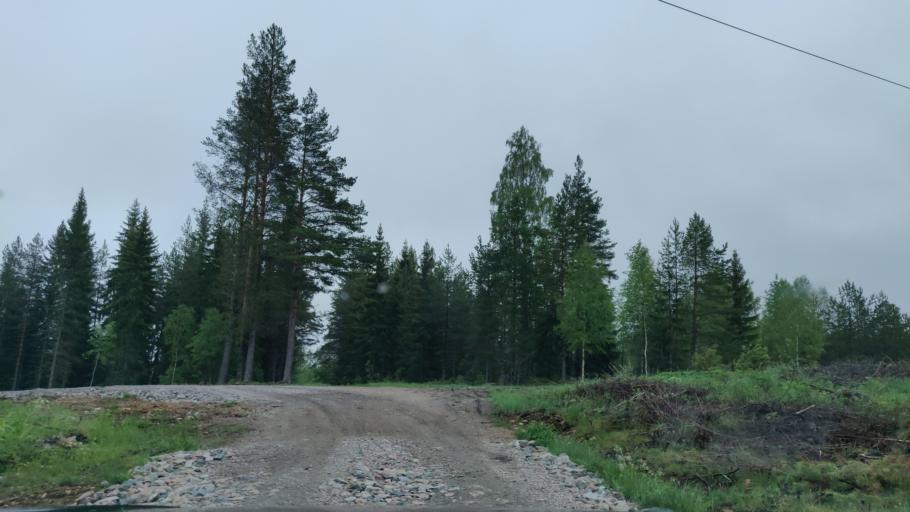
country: SE
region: Dalarna
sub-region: Avesta Kommun
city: Horndal
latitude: 60.3050
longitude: 16.4028
